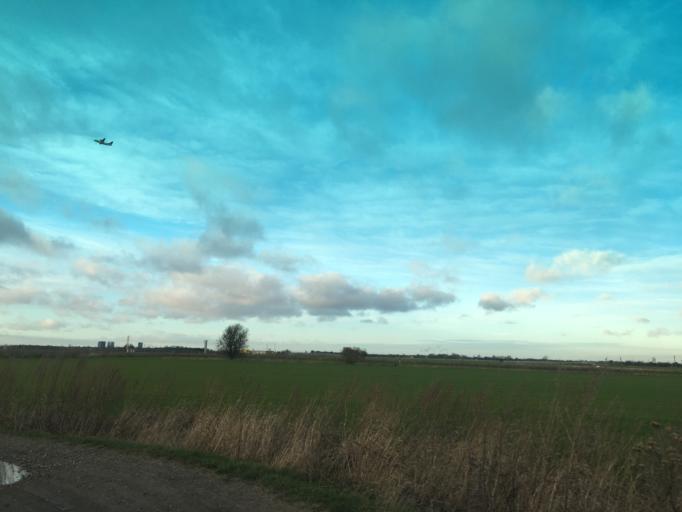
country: DK
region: Capital Region
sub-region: Tarnby Kommune
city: Tarnby
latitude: 55.5888
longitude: 12.6120
